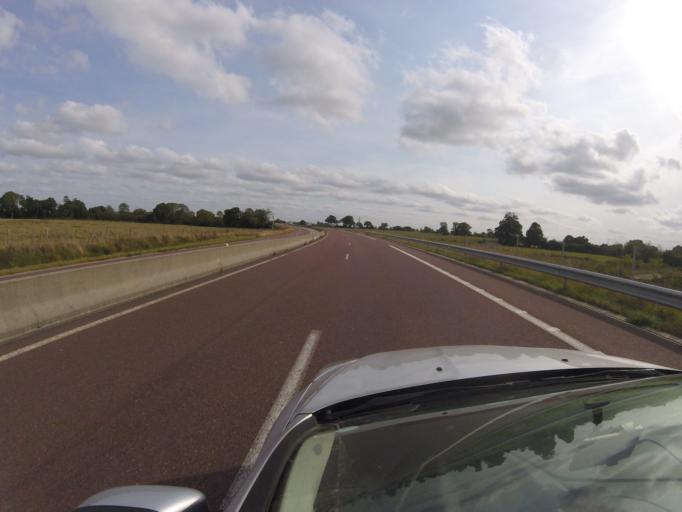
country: FR
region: Lower Normandy
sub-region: Departement de la Manche
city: Saint-Hilaire-Petitville
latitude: 49.2986
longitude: -1.1719
